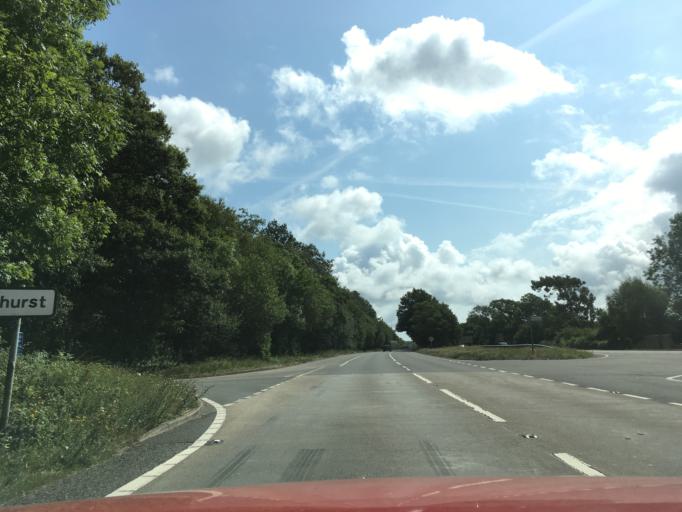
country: GB
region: England
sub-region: West Sussex
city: Rustington
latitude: 50.8429
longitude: -0.5147
